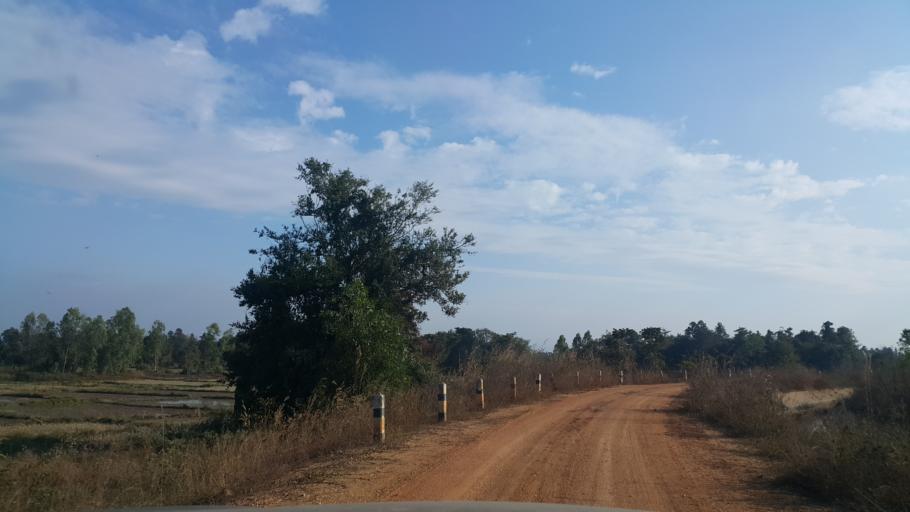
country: TH
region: Lampang
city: Ko Kha
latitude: 18.2560
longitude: 99.3665
